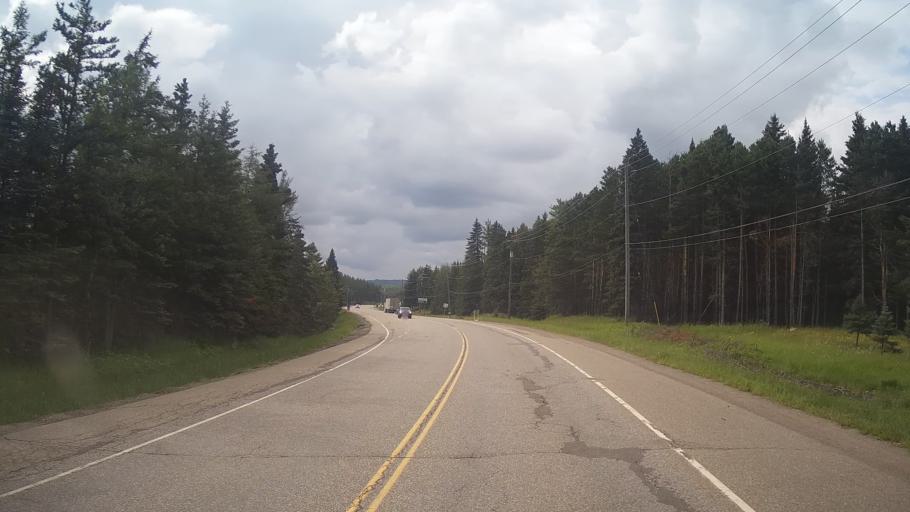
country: CA
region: Ontario
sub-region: Thunder Bay District
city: Thunder Bay
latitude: 48.4795
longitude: -89.3194
